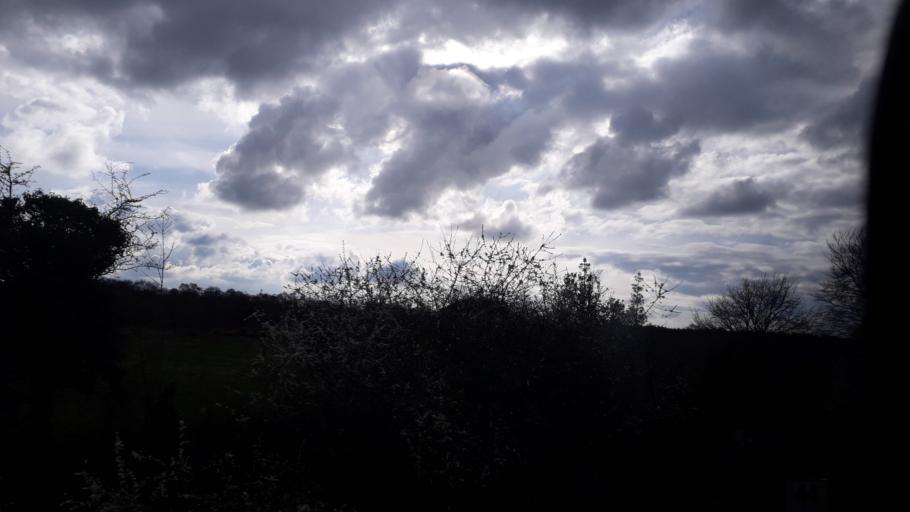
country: IE
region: Leinster
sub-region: An Iarmhi
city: Rathwire
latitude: 53.4927
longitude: -7.2198
